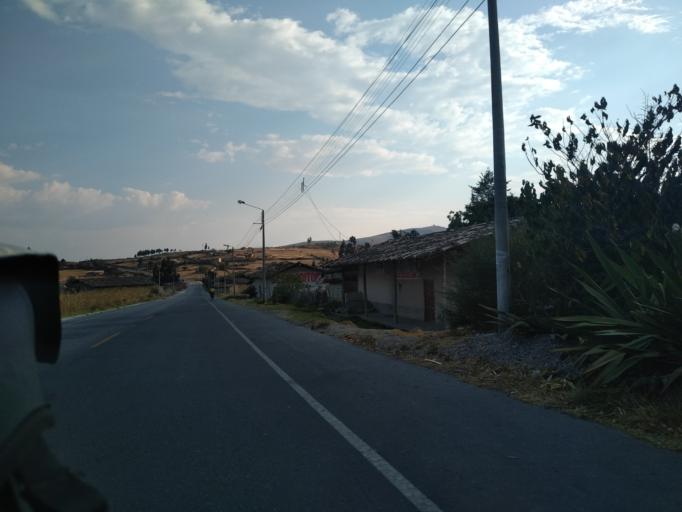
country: PE
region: Cajamarca
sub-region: San Marcos
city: La Grama
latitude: -7.3935
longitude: -78.1241
